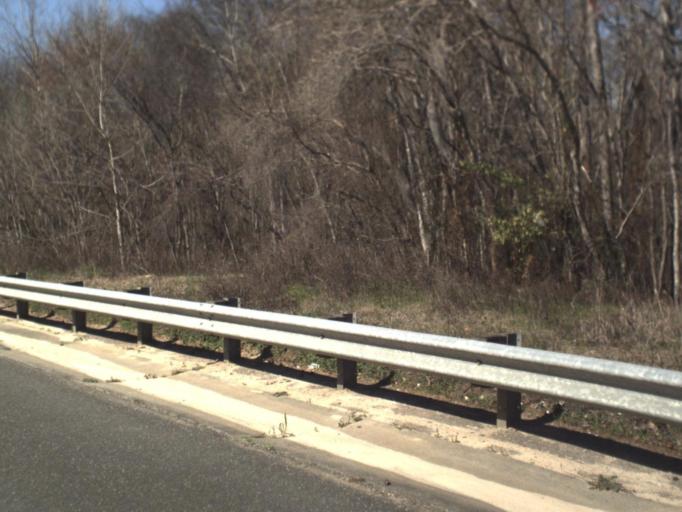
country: US
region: Florida
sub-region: Gadsden County
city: Chattahoochee
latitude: 30.6998
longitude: -84.8621
